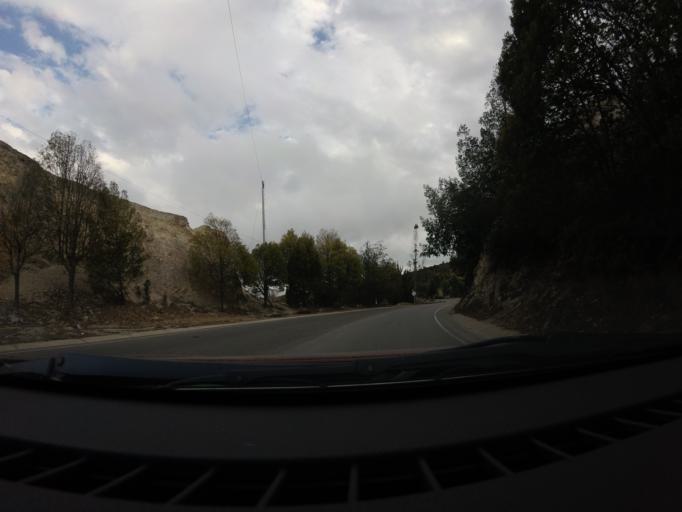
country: CO
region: Boyaca
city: Cucaita
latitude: 5.5625
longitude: -73.4142
